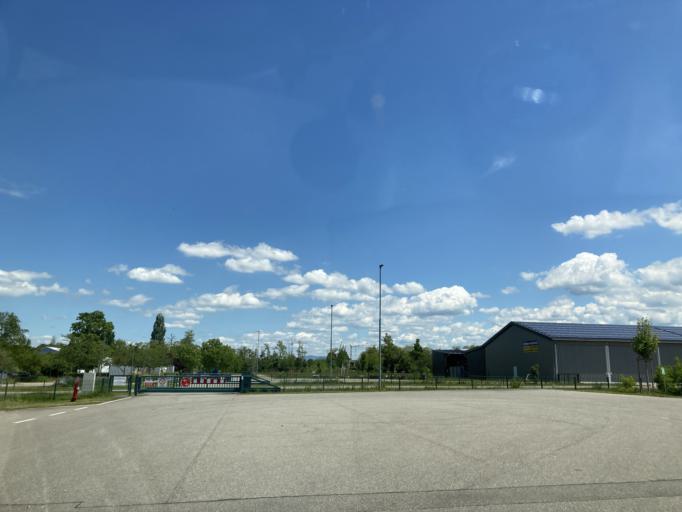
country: DE
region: Baden-Wuerttemberg
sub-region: Freiburg Region
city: Eschbach
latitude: 47.8981
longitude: 7.6219
